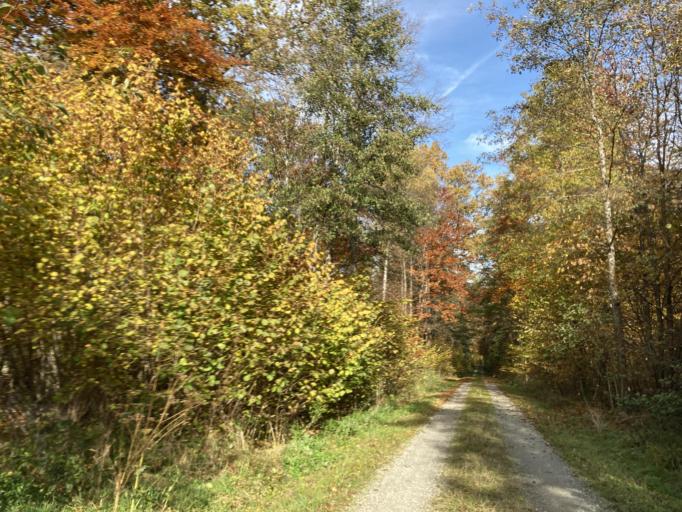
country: DE
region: Baden-Wuerttemberg
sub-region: Tuebingen Region
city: Bodelshausen
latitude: 48.4371
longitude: 8.9671
